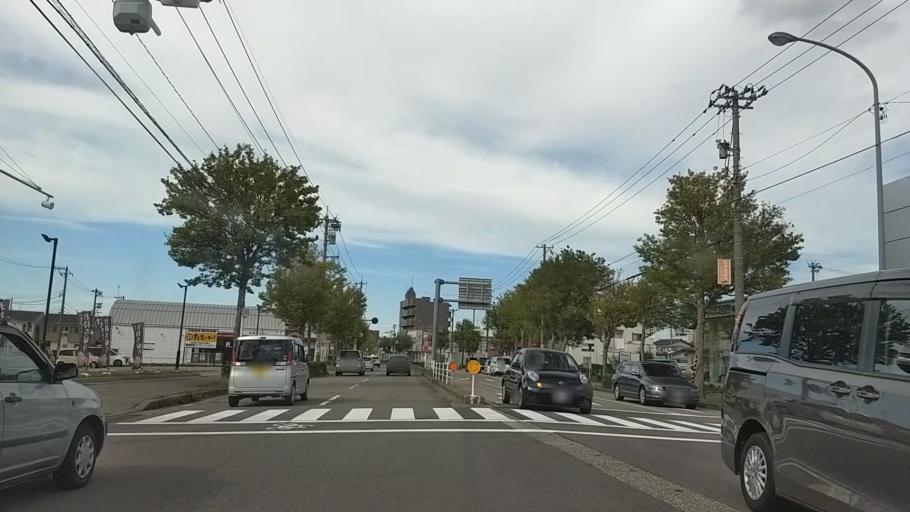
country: JP
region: Ishikawa
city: Nonoichi
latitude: 36.5345
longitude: 136.6390
